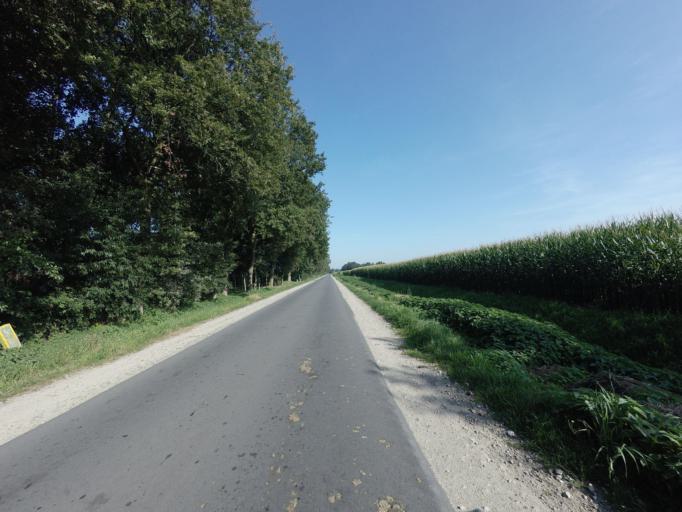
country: DE
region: Lower Saxony
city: Laar
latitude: 52.5848
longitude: 6.7797
